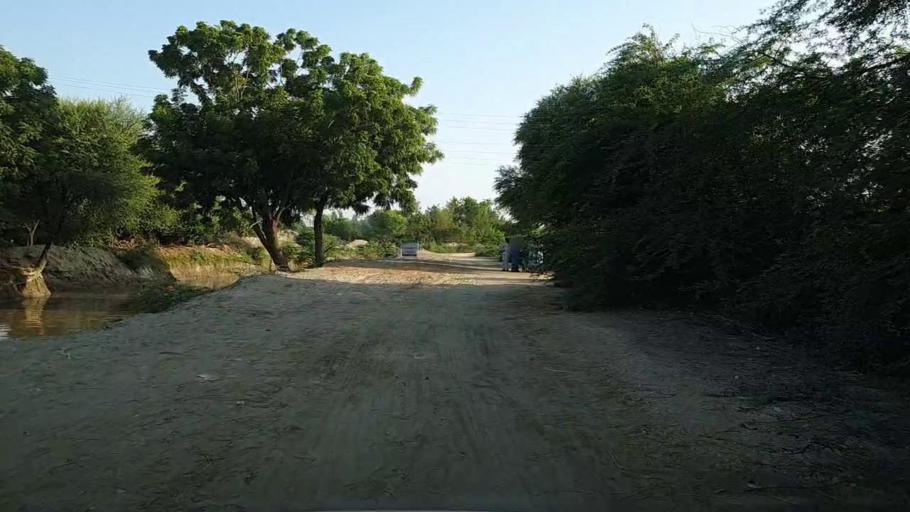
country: PK
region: Sindh
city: Kario
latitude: 24.7302
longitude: 68.6692
